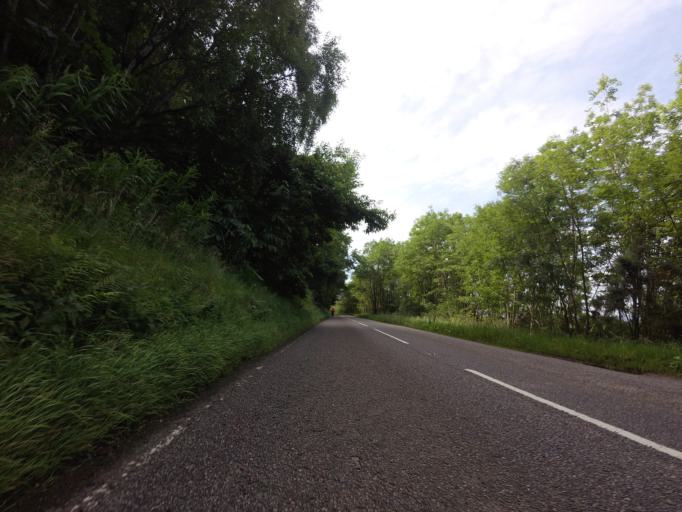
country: GB
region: Scotland
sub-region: Highland
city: Tain
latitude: 57.8279
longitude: -4.1288
